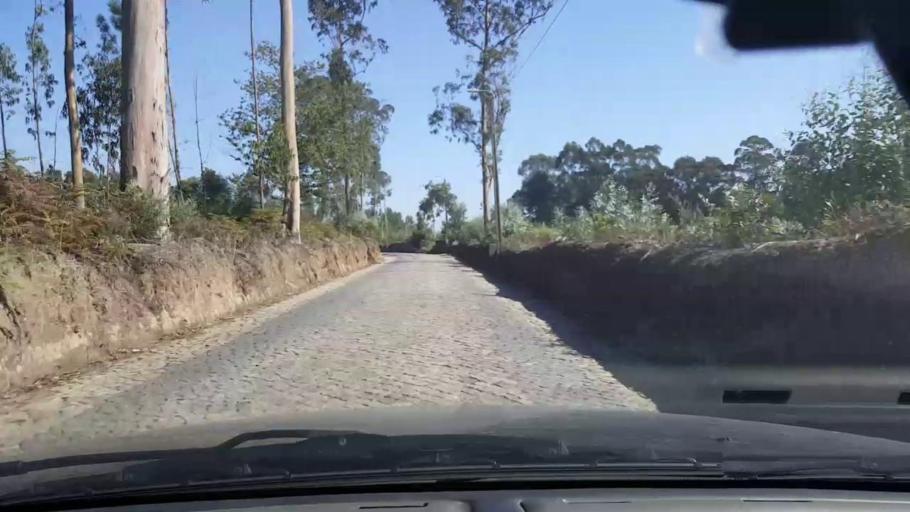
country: PT
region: Porto
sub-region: Matosinhos
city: Lavra
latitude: 41.2958
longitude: -8.7048
